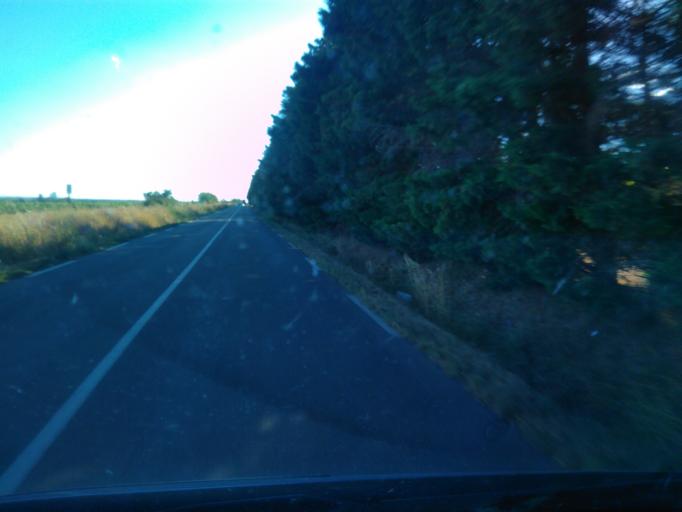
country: FR
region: Languedoc-Roussillon
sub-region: Departement du Gard
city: Beauvoisin
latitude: 43.6527
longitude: 4.3380
